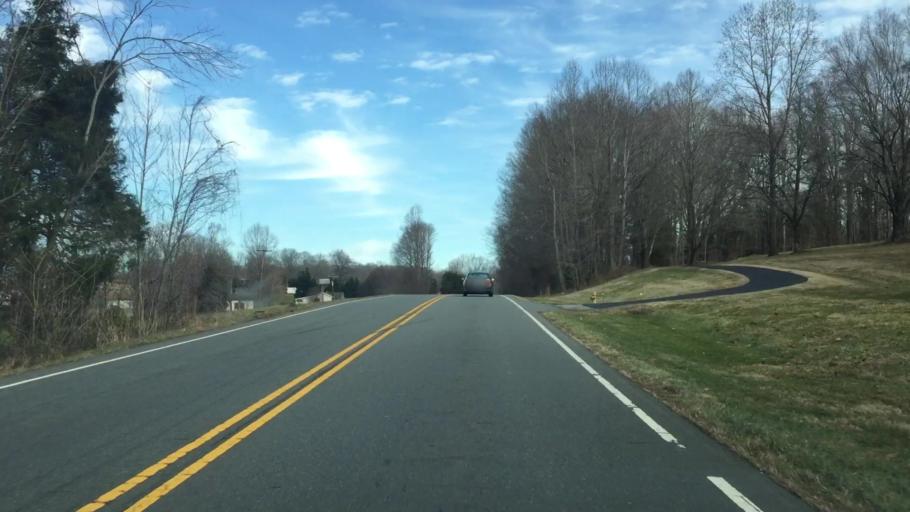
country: US
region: North Carolina
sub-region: Guilford County
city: Oak Ridge
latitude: 36.2098
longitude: -80.0692
